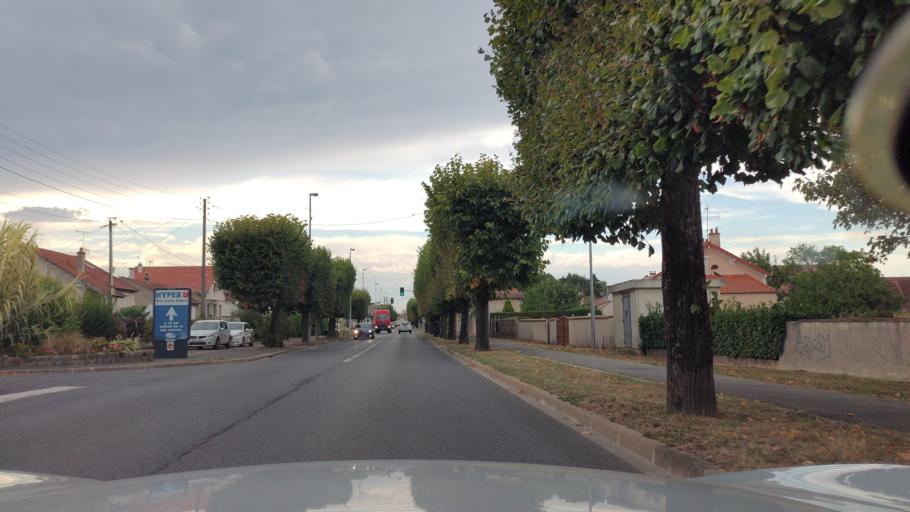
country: FR
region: Ile-de-France
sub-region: Departement de Seine-et-Marne
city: Guignes
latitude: 48.6325
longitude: 2.8064
